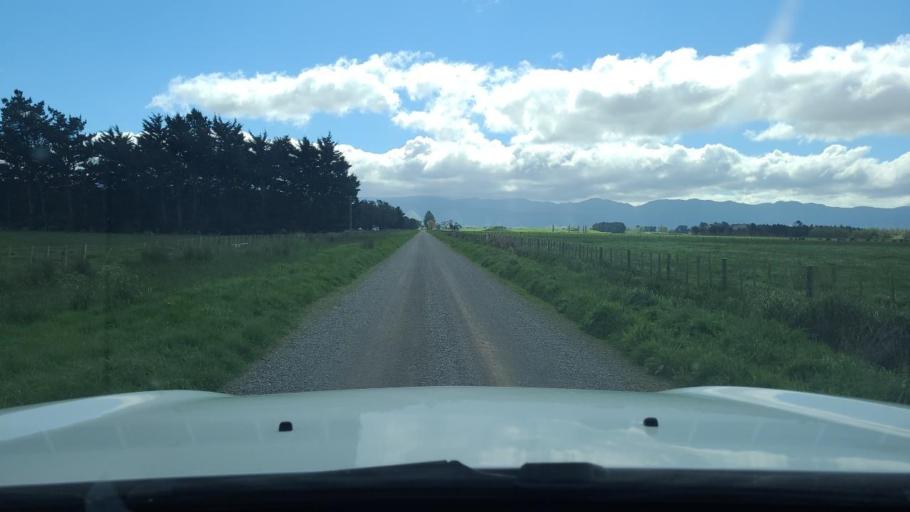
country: NZ
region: Wellington
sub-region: South Wairarapa District
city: Waipawa
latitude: -41.2438
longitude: 175.3080
